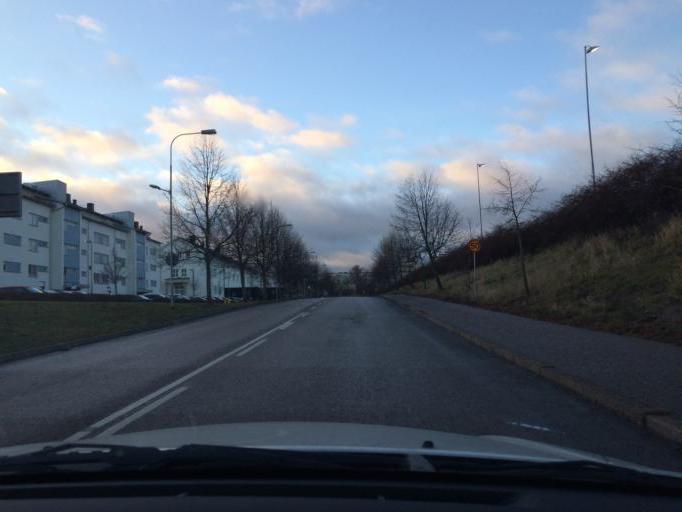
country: SE
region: Soedermanland
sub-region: Eskilstuna Kommun
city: Eskilstuna
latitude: 59.3669
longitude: 16.5138
